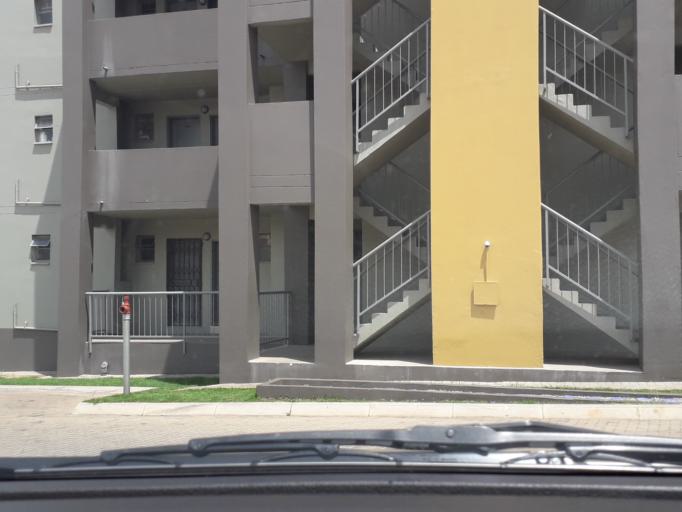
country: ZA
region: Gauteng
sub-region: City of Johannesburg Metropolitan Municipality
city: Roodepoort
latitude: -26.2053
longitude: 27.9113
